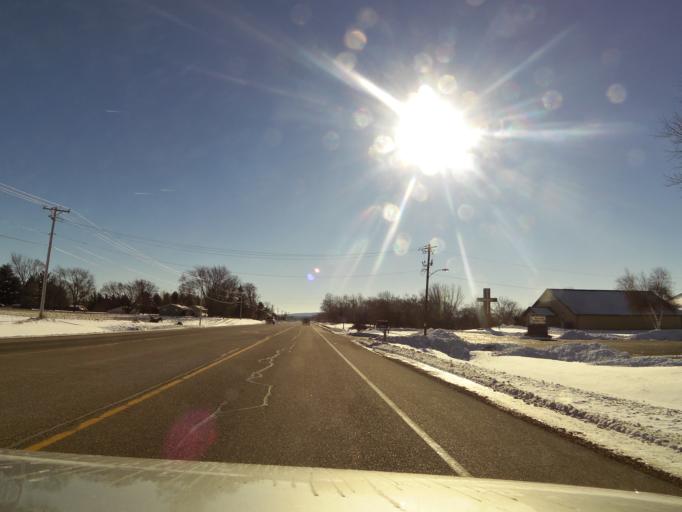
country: US
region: Wisconsin
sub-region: Sauk County
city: West Baraboo
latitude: 43.5018
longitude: -89.7784
